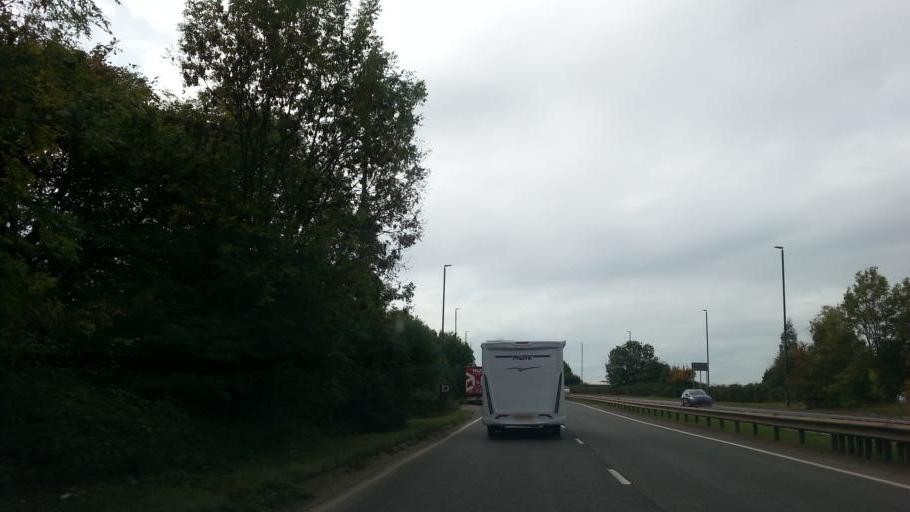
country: GB
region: England
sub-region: Gloucestershire
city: Stonehouse
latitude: 51.8106
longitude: -2.2848
